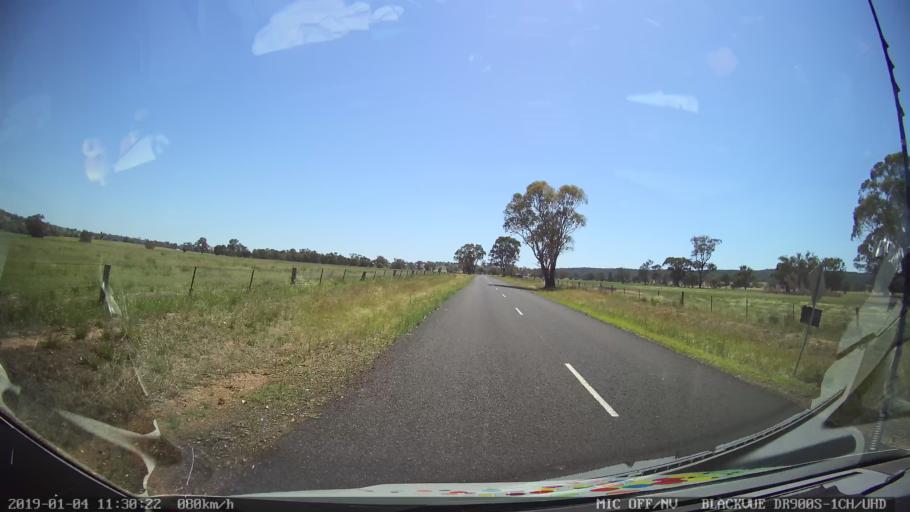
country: AU
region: New South Wales
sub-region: Cabonne
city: Molong
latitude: -33.0783
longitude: 148.7804
